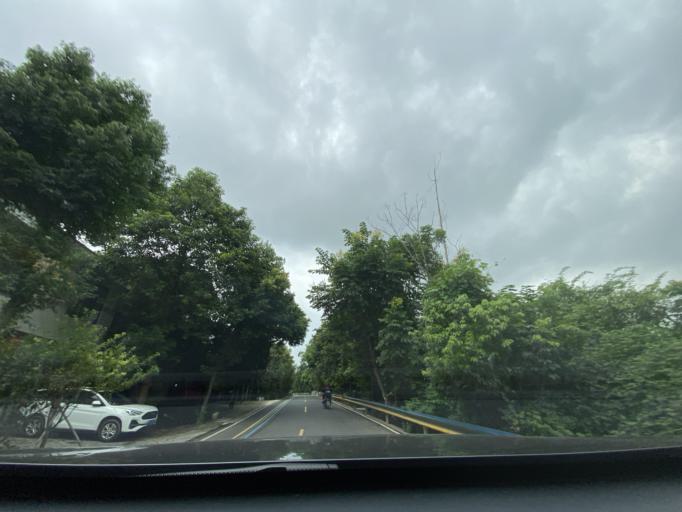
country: CN
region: Sichuan
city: Dongsheng
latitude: 30.4097
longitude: 103.9958
